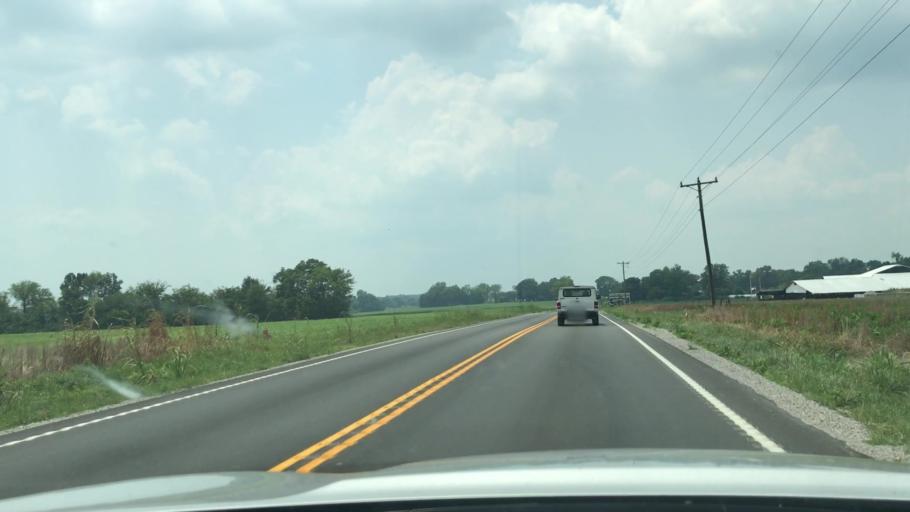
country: US
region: Kentucky
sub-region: Todd County
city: Guthrie
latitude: 36.6553
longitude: -87.1802
